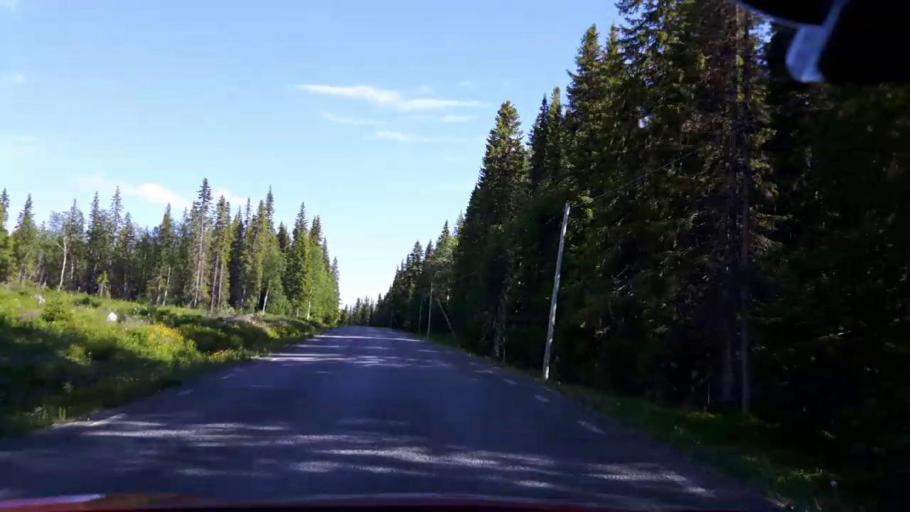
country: SE
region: Jaemtland
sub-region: Krokoms Kommun
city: Valla
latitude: 63.7222
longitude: 14.1239
